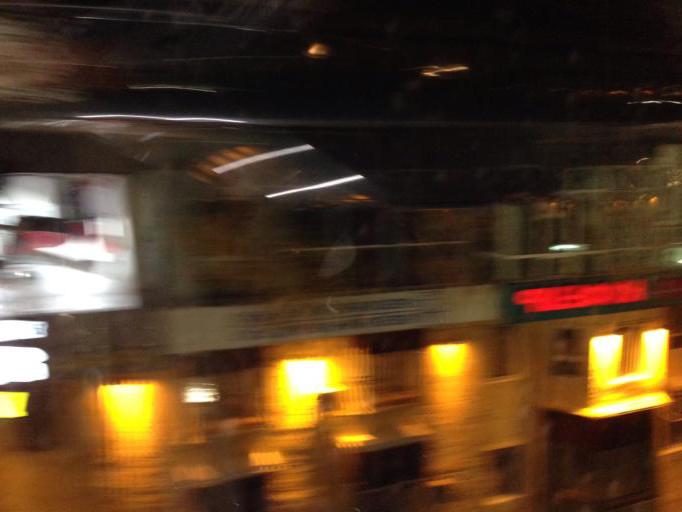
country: KZ
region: Astana Qalasy
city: Astana
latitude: 51.1841
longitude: 71.4165
